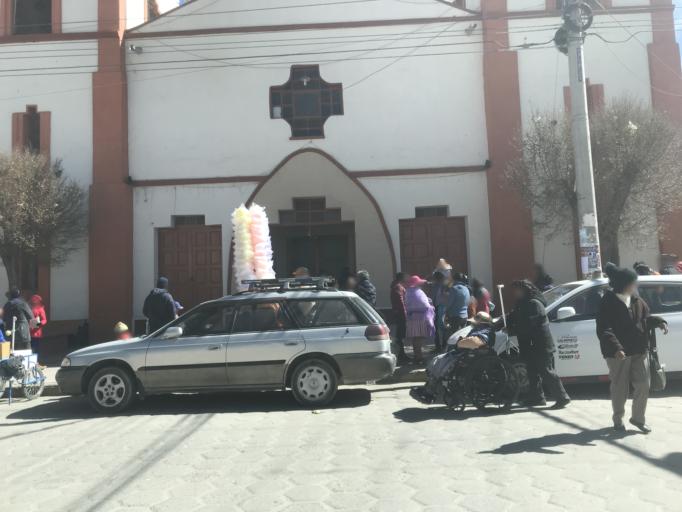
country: BO
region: Potosi
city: Uyuni
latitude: -20.4620
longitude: -66.8249
